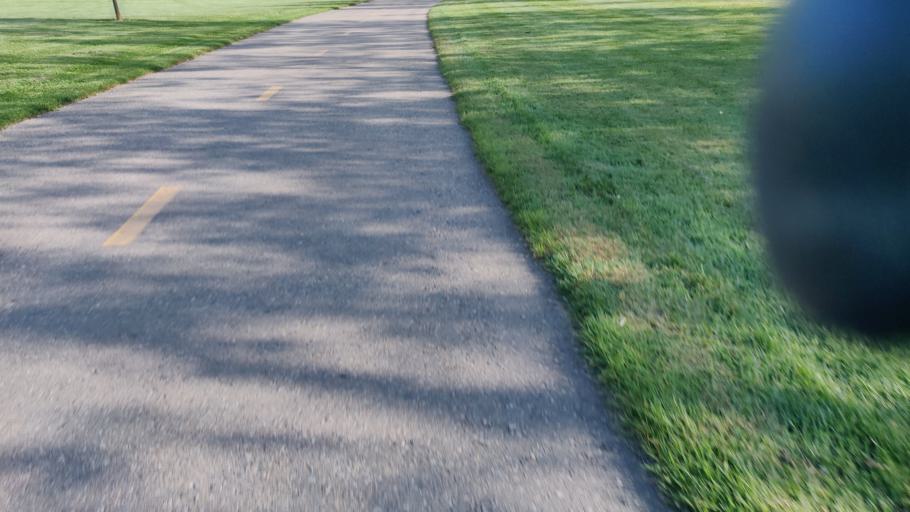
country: US
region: Idaho
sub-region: Ada County
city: Boise
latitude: 43.5732
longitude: -116.1447
